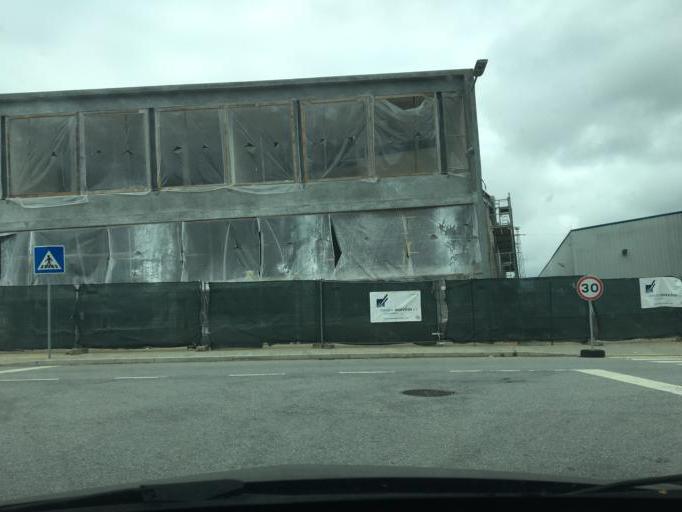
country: PT
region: Porto
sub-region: Matosinhos
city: Santa Cruz do Bispo
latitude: 41.2353
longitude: -8.6646
